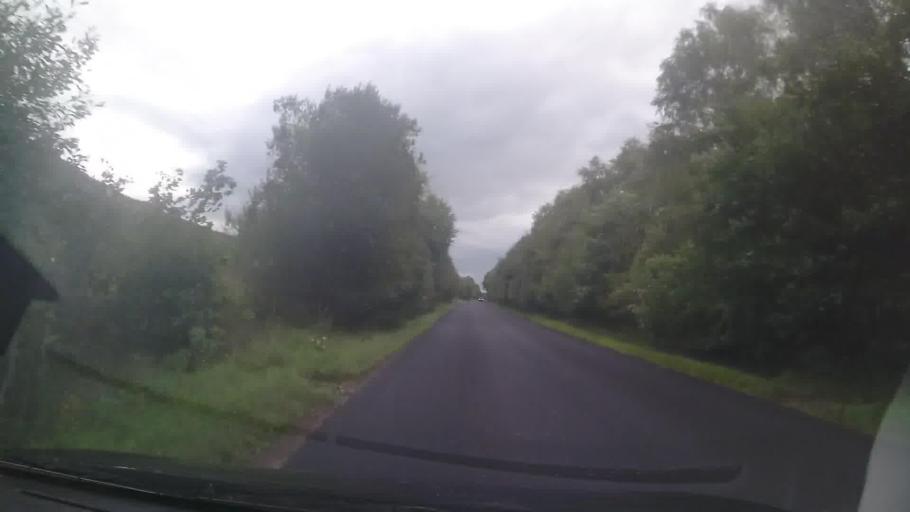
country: GB
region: Scotland
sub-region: Argyll and Bute
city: Garelochhead
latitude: 56.2403
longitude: -4.9563
